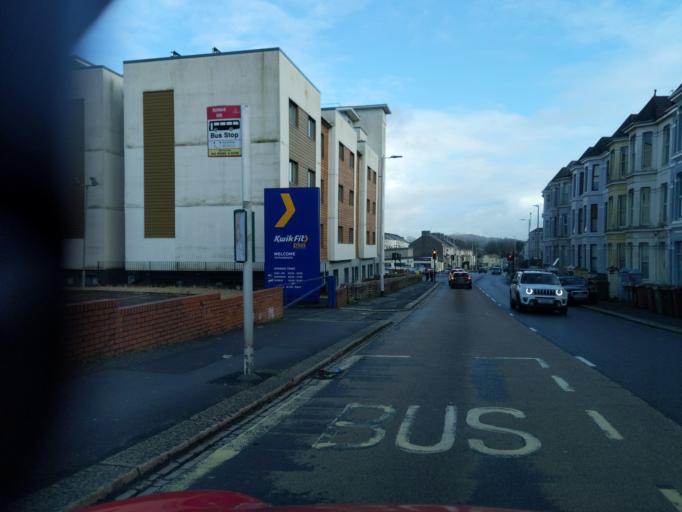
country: GB
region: England
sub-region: Plymouth
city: Plymouth
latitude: 50.3819
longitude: -4.1258
